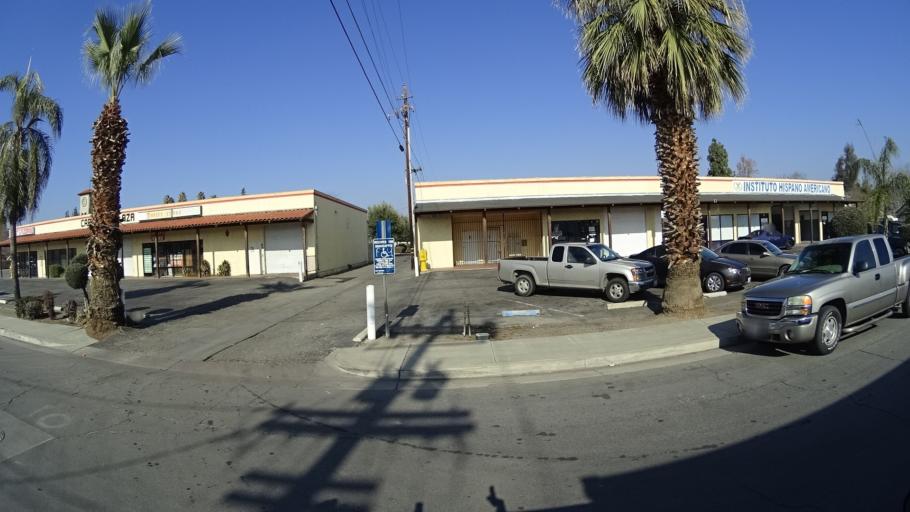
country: US
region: California
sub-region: Kern County
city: Bakersfield
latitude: 35.3923
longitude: -119.0181
